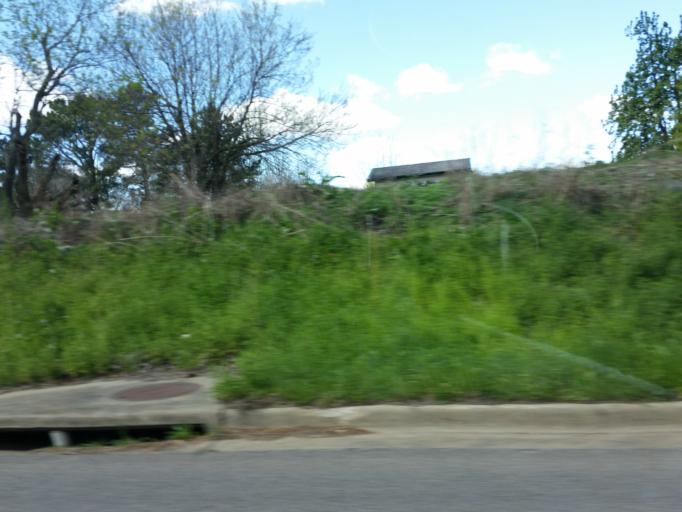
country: US
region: Arkansas
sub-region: Craighead County
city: Jonesboro
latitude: 35.8689
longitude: -90.7030
